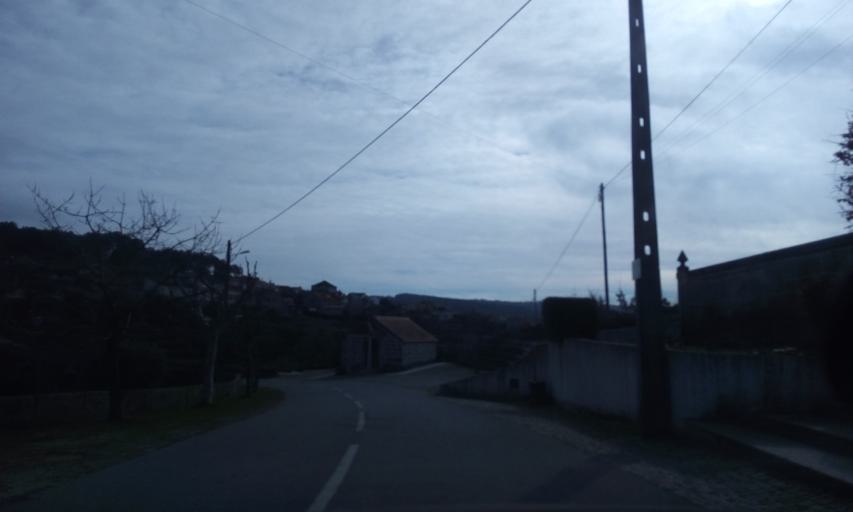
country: PT
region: Guarda
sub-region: Fornos de Algodres
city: Fornos de Algodres
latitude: 40.6827
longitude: -7.5333
